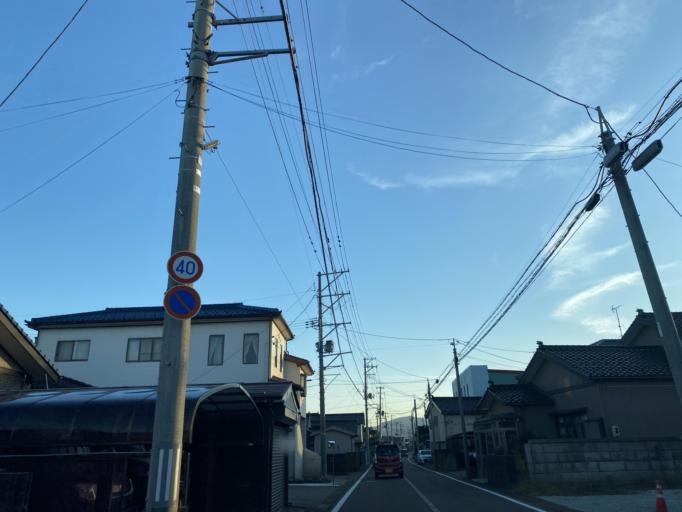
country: JP
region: Niigata
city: Kashiwazaki
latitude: 37.3832
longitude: 138.5687
